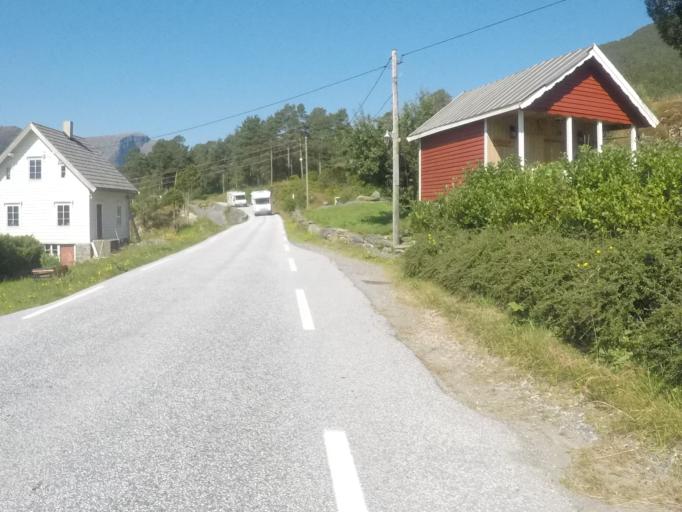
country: NO
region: Sogn og Fjordane
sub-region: Bremanger
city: Svelgen
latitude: 61.7390
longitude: 5.1754
